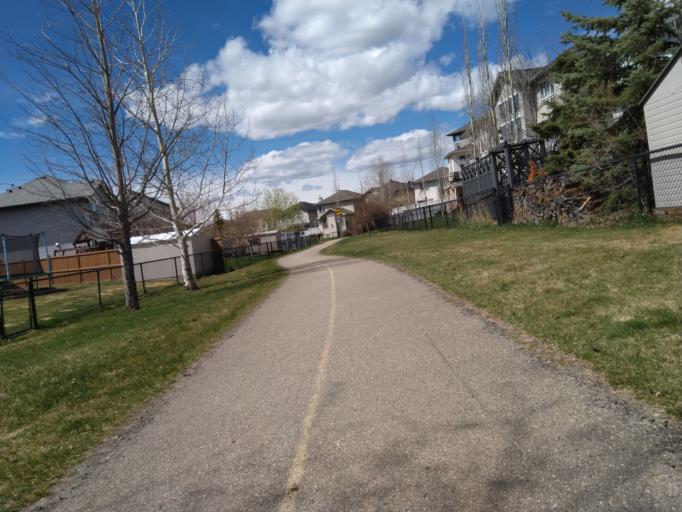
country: CA
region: Alberta
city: Calgary
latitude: 51.1157
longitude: -114.2386
